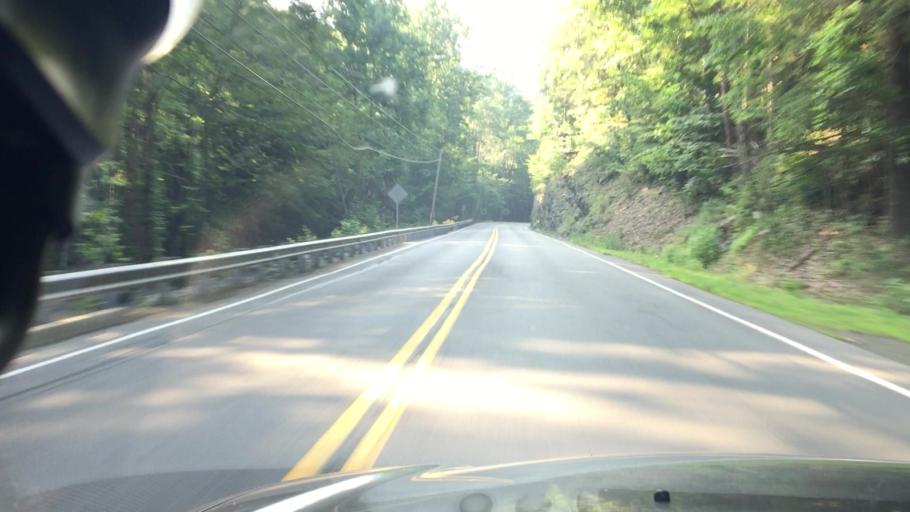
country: US
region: Pennsylvania
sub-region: Northumberland County
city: Elysburg
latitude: 40.8869
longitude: -76.5073
